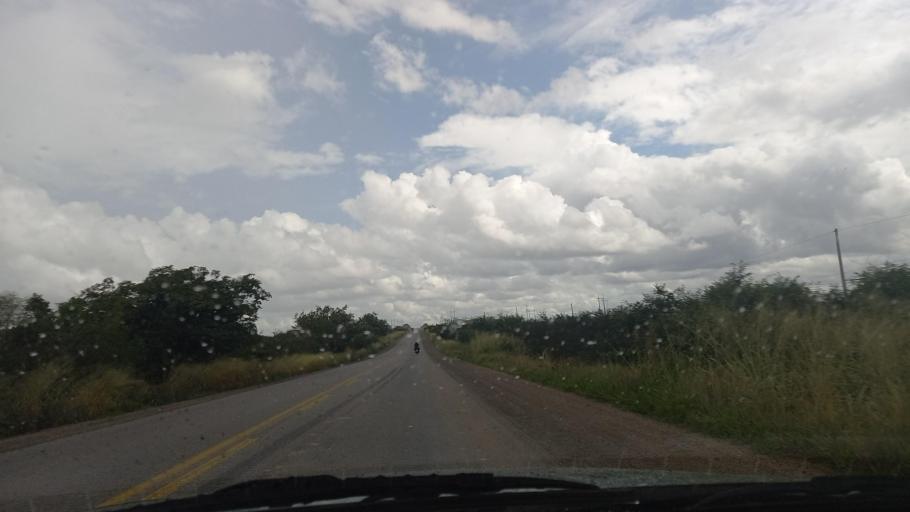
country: BR
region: Pernambuco
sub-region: Cachoeirinha
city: Cachoeirinha
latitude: -8.5624
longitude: -36.2772
